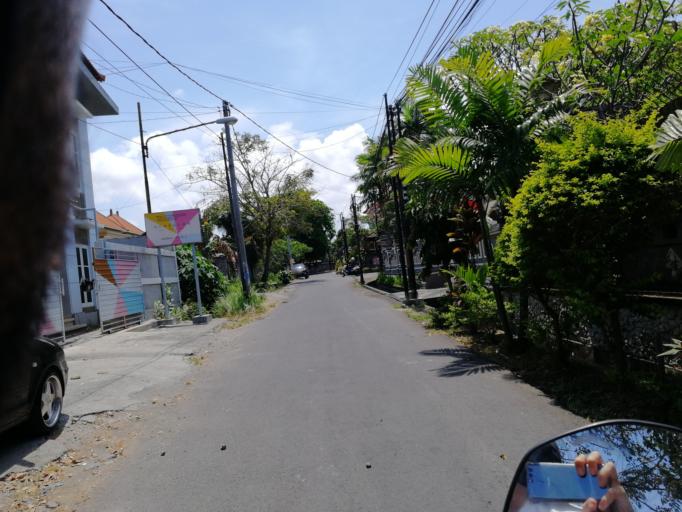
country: ID
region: Bali
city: Dajan Tangluk
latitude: -8.6651
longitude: 115.2346
